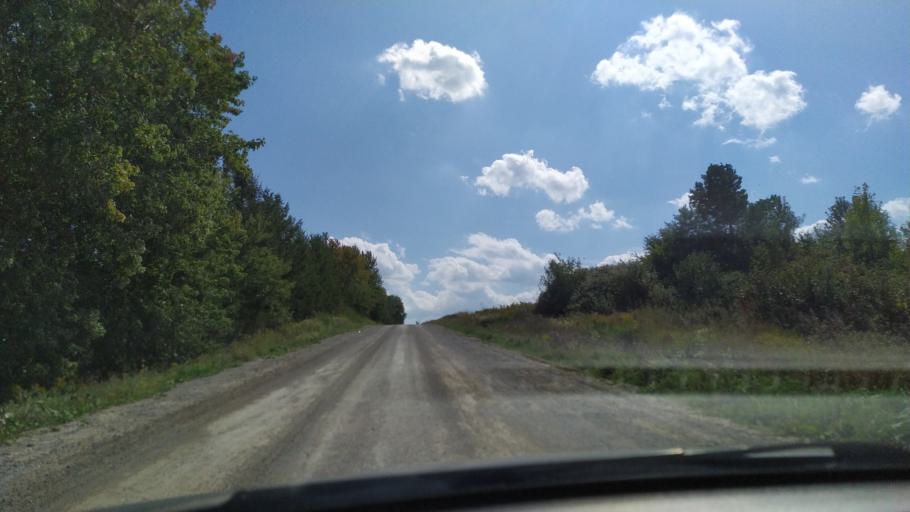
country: CA
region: Ontario
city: Stratford
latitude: 43.2898
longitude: -80.9312
